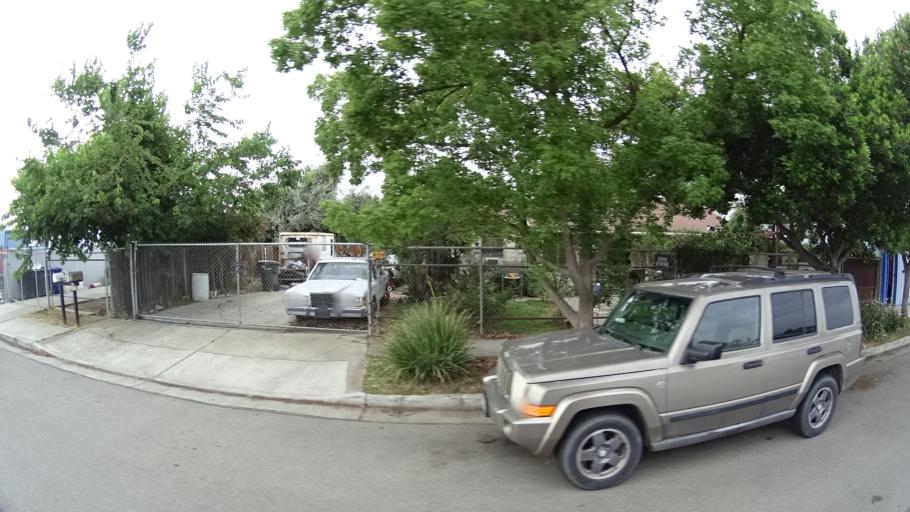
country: US
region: California
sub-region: Kings County
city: Hanford
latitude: 36.3255
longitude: -119.6394
